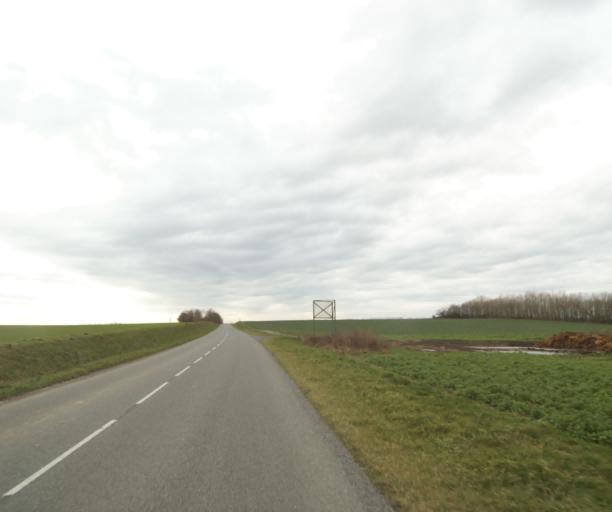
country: FR
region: Nord-Pas-de-Calais
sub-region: Departement du Nord
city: Sebourg
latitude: 50.3314
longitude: 3.6347
